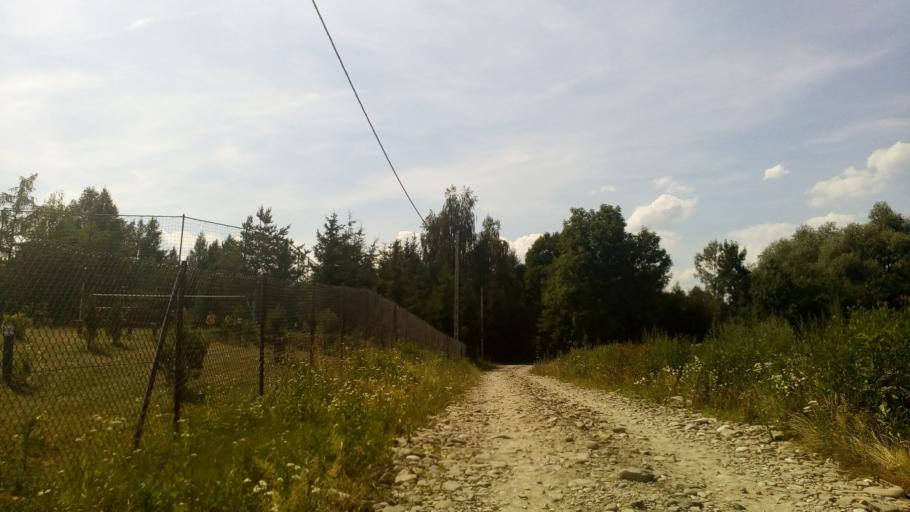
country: PL
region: Lesser Poland Voivodeship
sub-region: Powiat nowosadecki
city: Stary Sacz
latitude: 49.5823
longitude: 20.6428
